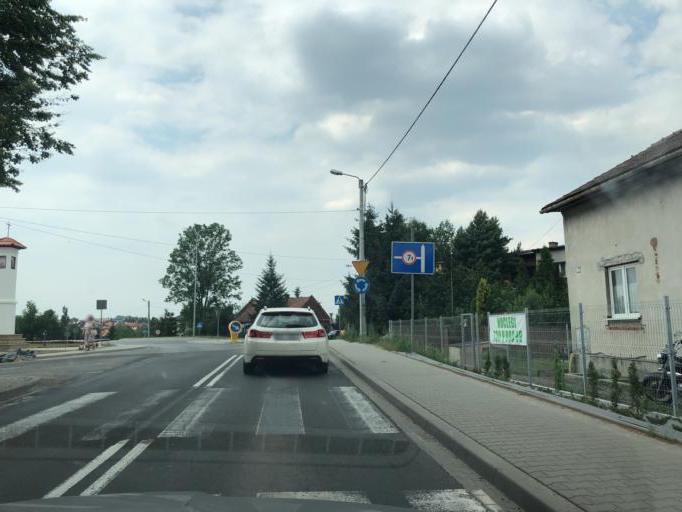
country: PL
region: Lesser Poland Voivodeship
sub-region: Powiat wielicki
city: Wieliczka
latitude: 49.9885
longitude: 20.0427
